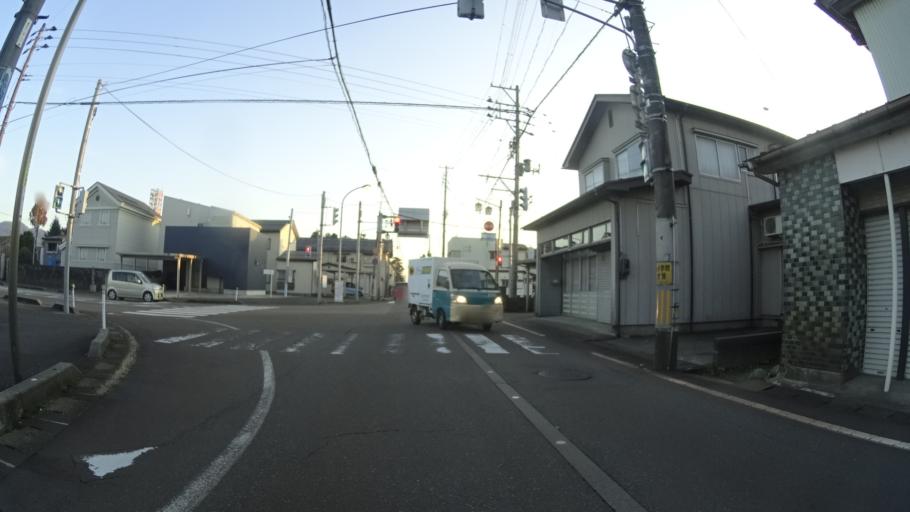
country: JP
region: Niigata
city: Nagaoka
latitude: 37.4177
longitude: 138.8410
